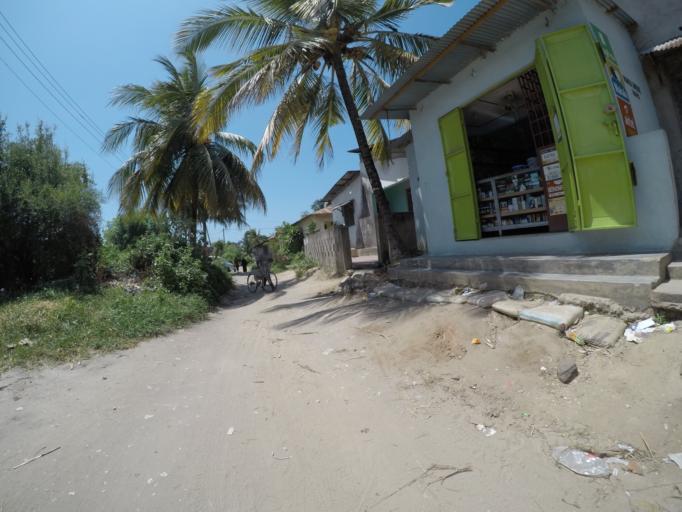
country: TZ
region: Zanzibar Urban/West
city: Zanzibar
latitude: -6.1786
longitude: 39.2069
